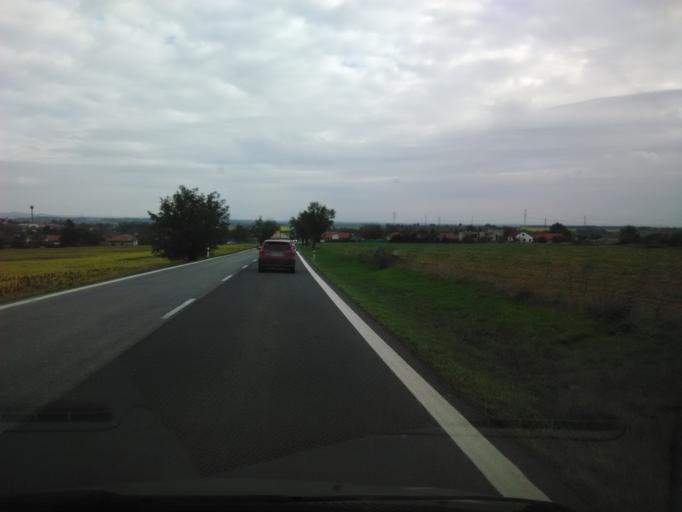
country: SK
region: Nitriansky
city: Tlmace
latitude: 48.2133
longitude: 18.4555
